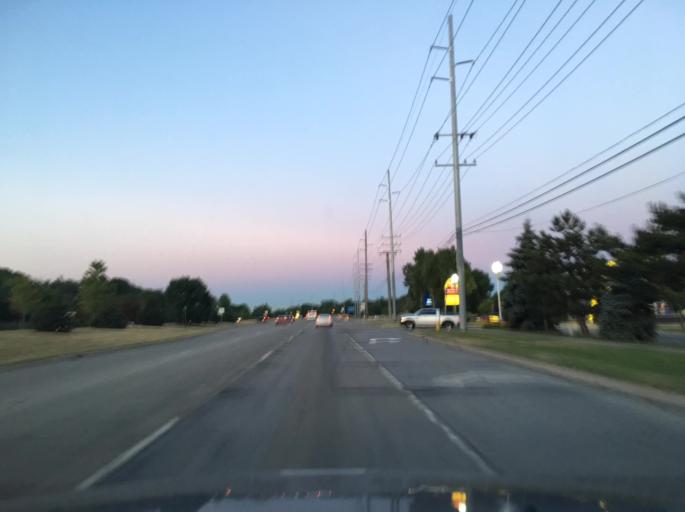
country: US
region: Michigan
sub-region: Macomb County
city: Mount Clemens
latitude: 42.6286
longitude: -82.8947
